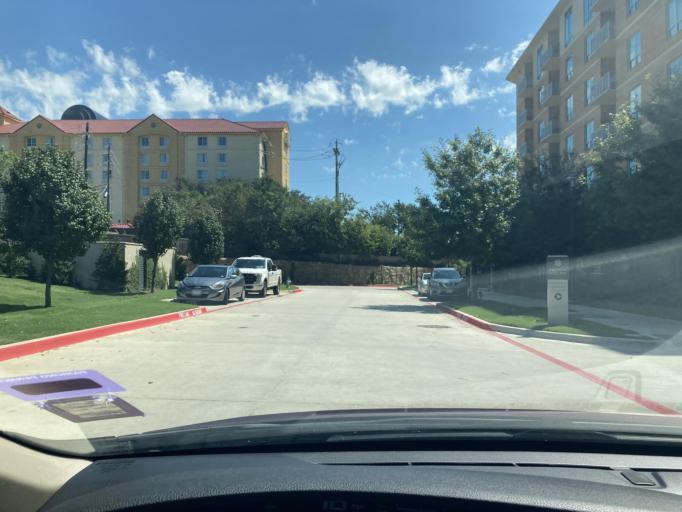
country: US
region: Texas
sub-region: Dallas County
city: University Park
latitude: 32.8827
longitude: -96.7719
